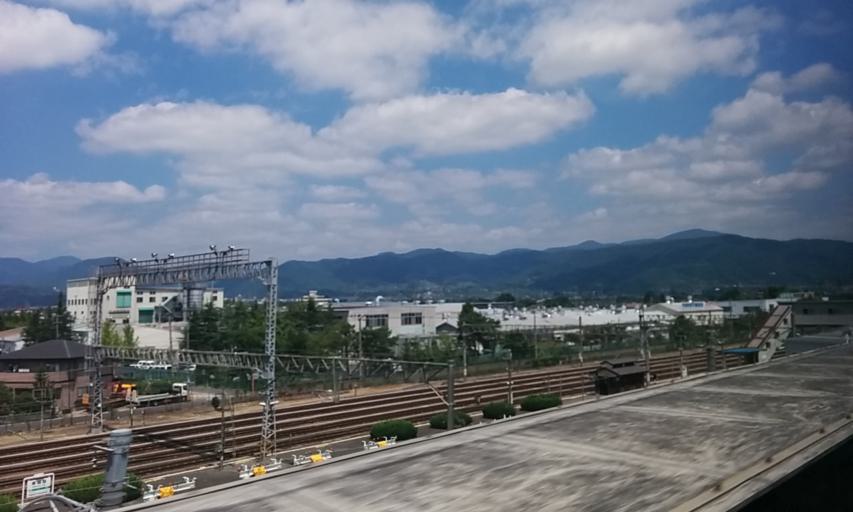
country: JP
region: Fukushima
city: Fukushima-shi
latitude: 37.7991
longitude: 140.4775
